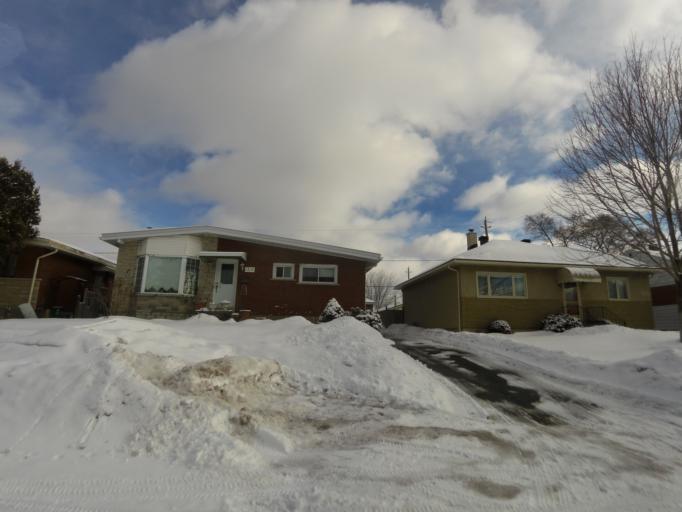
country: CA
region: Ontario
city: Ottawa
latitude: 45.4183
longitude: -75.6423
